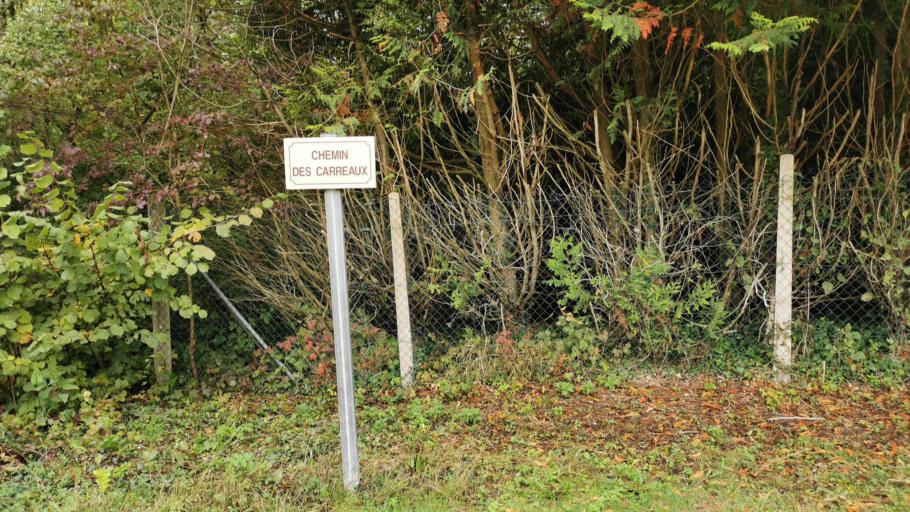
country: FR
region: Champagne-Ardenne
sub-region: Departement de l'Aube
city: Romilly-sur-Seine
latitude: 48.5208
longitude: 3.6478
